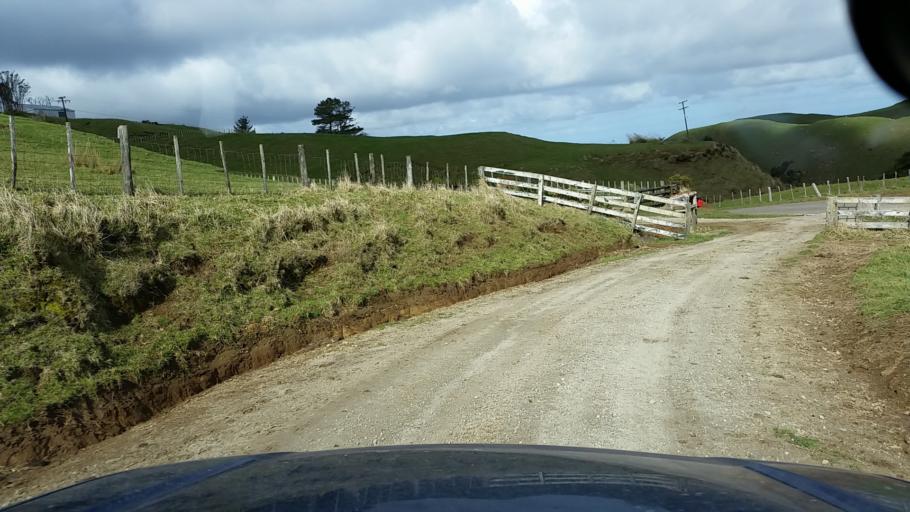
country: NZ
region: Taranaki
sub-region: South Taranaki District
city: Patea
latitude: -39.6695
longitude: 174.5654
